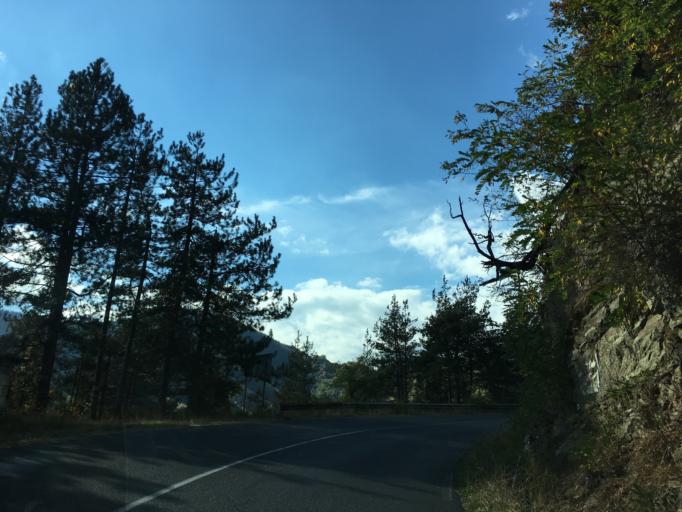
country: BG
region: Smolyan
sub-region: Obshtina Madan
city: Madan
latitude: 41.4476
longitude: 24.9952
